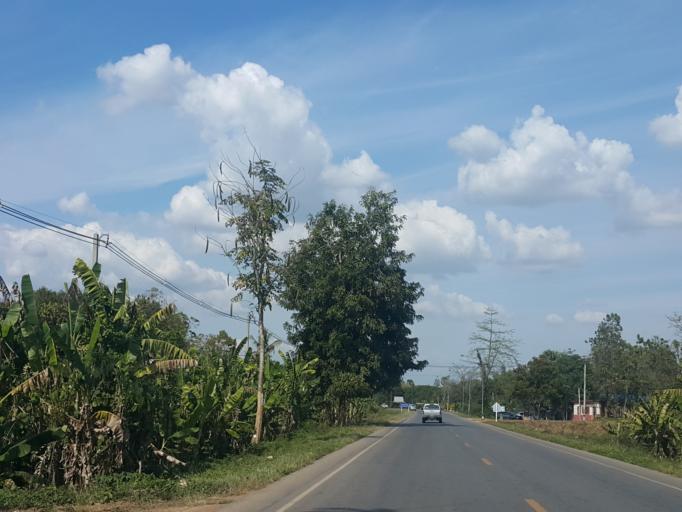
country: TH
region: Sukhothai
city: Sawankhalok
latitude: 17.2419
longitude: 99.8469
